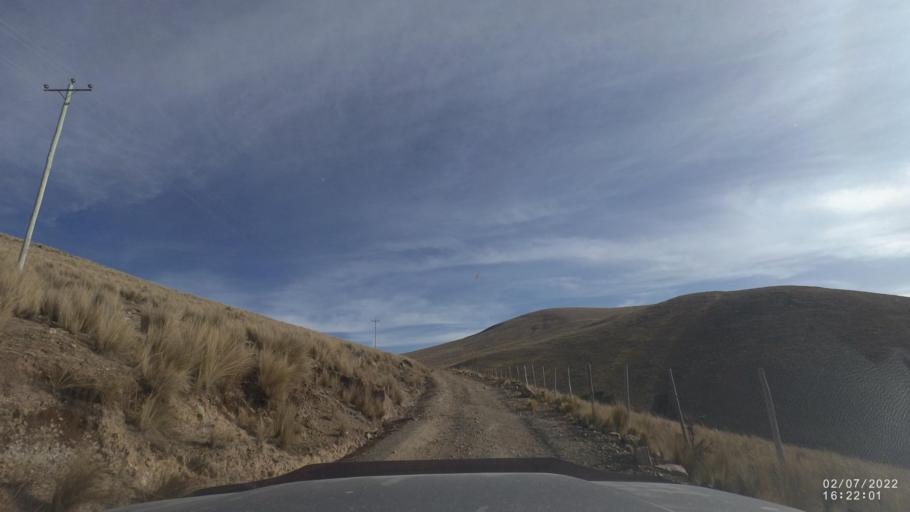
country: BO
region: Cochabamba
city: Irpa Irpa
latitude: -17.9320
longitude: -66.4529
